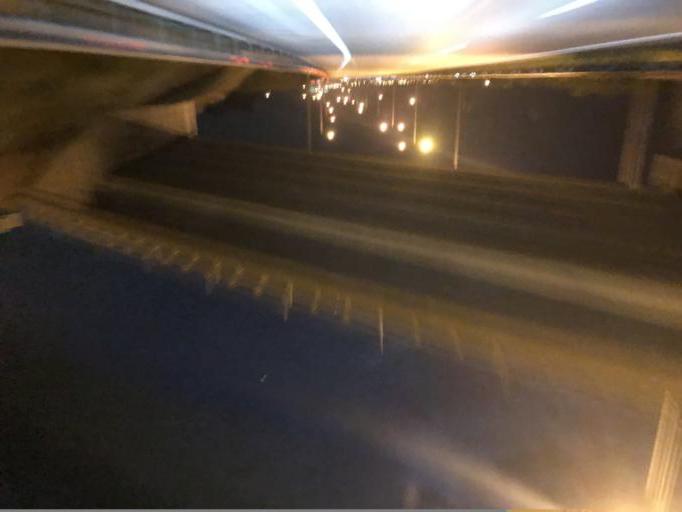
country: TR
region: Hatay
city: Mahmutlar
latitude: 36.9639
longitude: 36.1131
